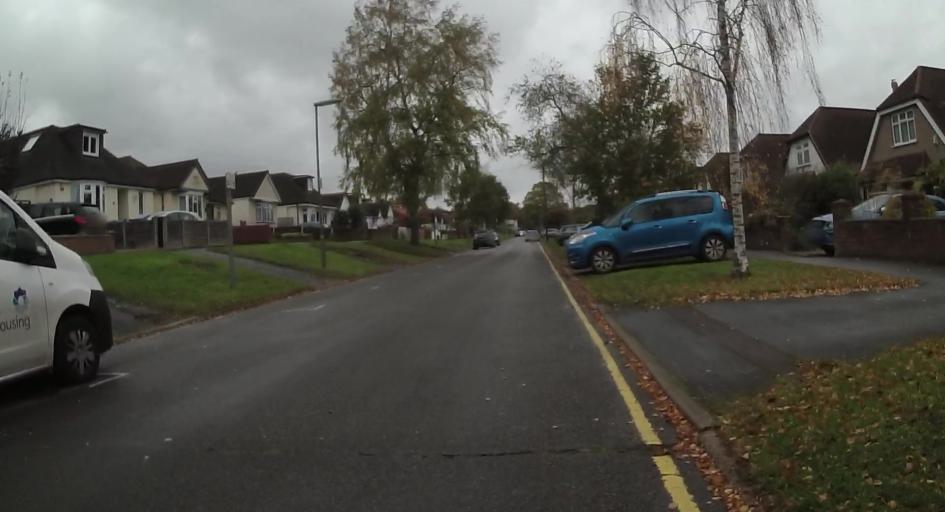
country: GB
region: England
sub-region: Surrey
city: West Byfleet
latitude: 51.3392
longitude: -0.5106
